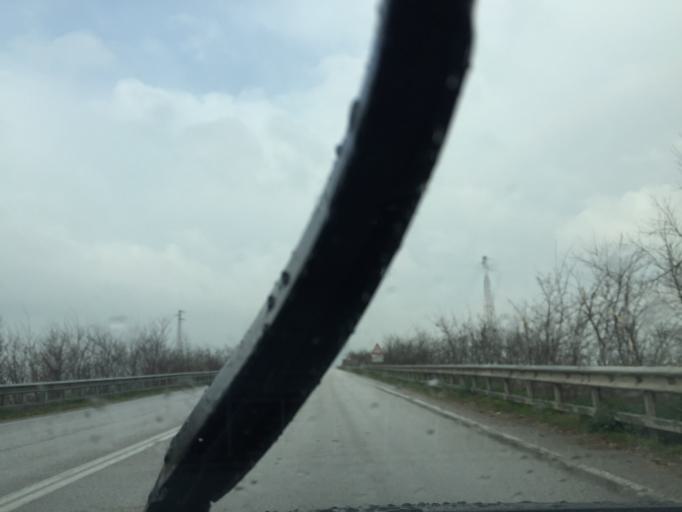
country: IT
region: Apulia
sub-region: Provincia di Foggia
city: Foggia
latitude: 41.4983
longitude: 15.5362
